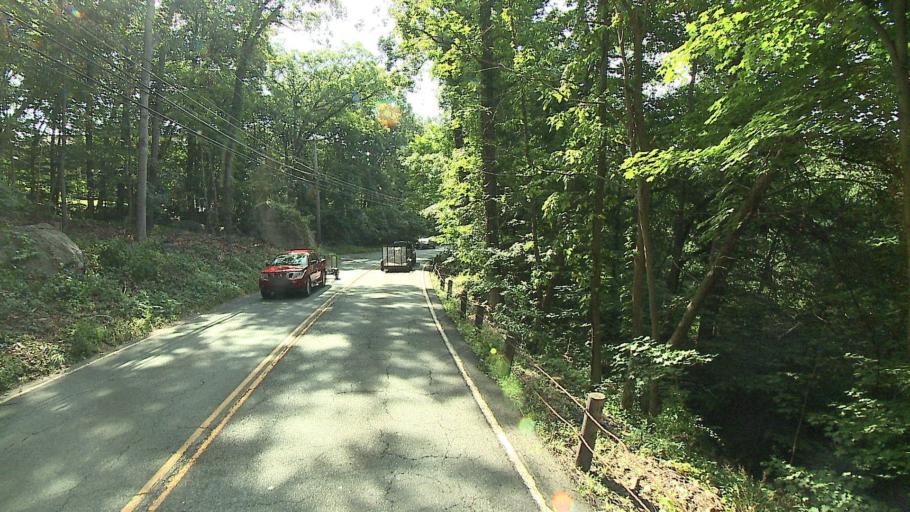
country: US
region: Connecticut
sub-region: Fairfield County
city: Danbury
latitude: 41.4225
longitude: -73.4695
